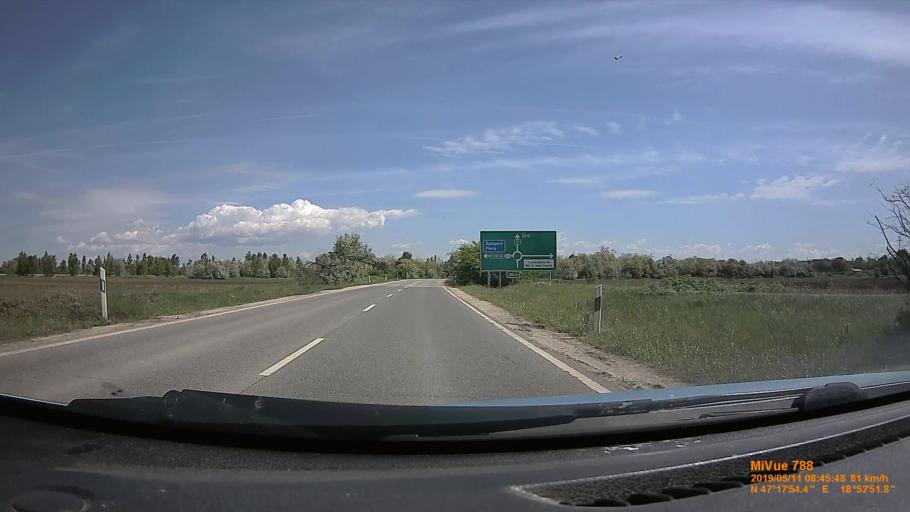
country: HU
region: Pest
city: Szazhalombatta
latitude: 47.2986
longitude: 18.8813
